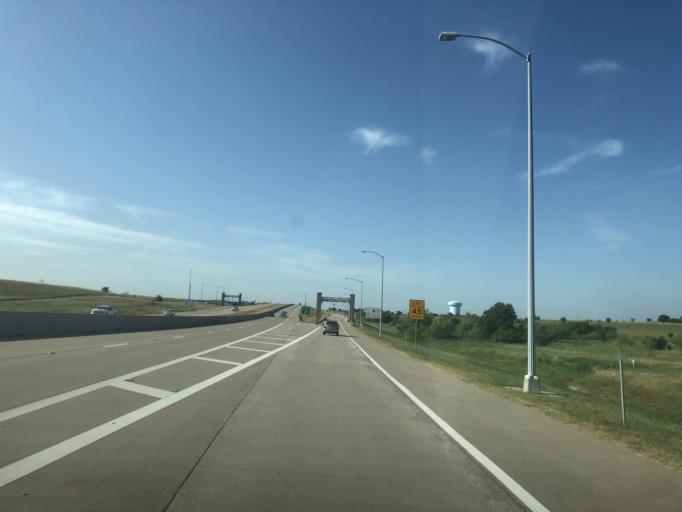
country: US
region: Texas
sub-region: Tarrant County
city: Crowley
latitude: 32.6129
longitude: -97.4128
